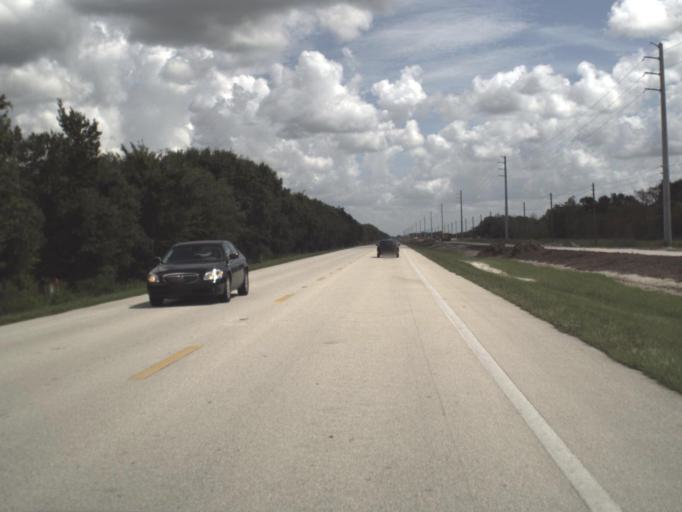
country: US
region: Florida
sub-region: DeSoto County
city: Nocatee
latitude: 27.1053
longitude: -81.9326
